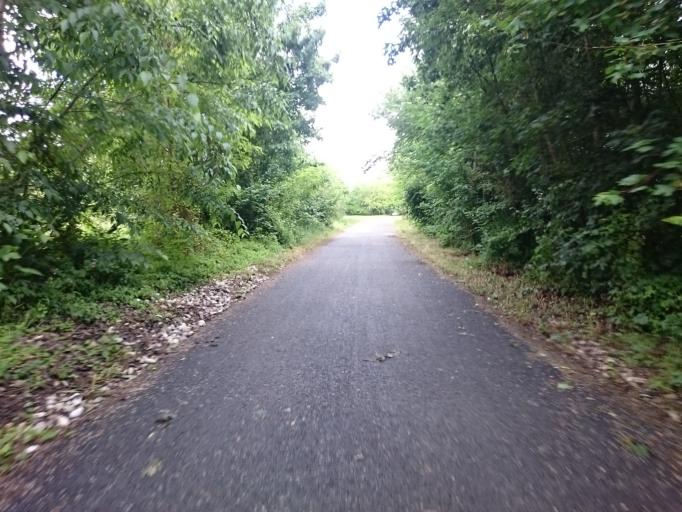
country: IT
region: Veneto
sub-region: Provincia di Padova
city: Campodoro
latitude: 45.5041
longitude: 11.7453
